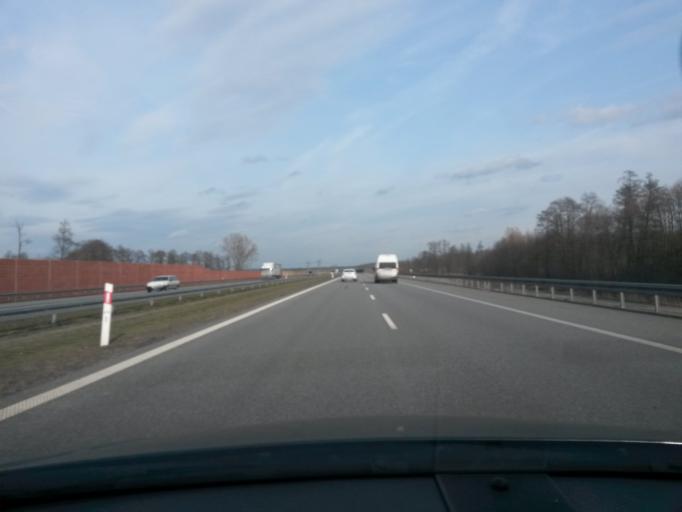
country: PL
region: Greater Poland Voivodeship
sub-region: Powiat koninski
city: Krzymow
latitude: 52.1423
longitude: 18.3889
